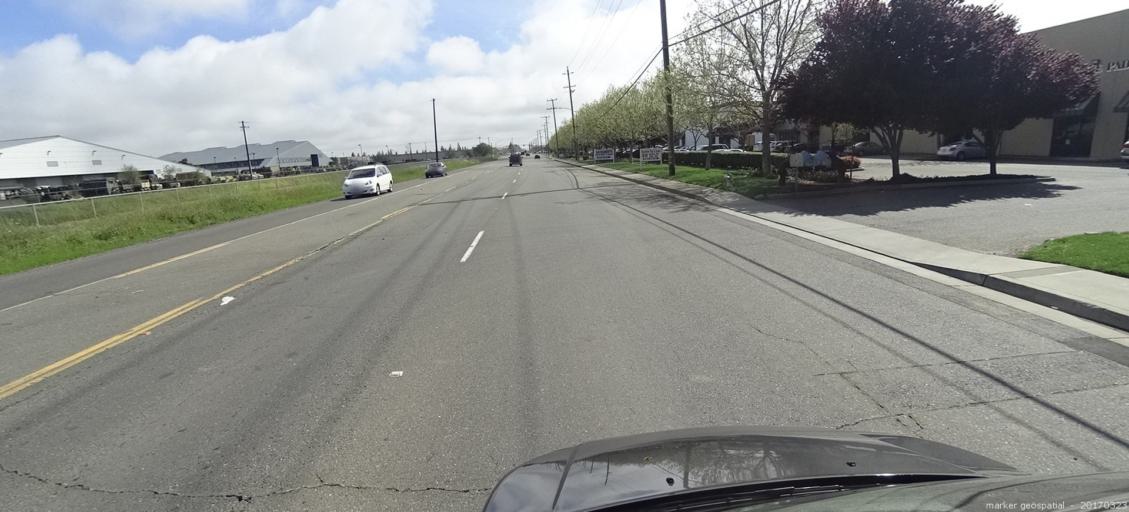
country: US
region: California
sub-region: Sacramento County
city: Florin
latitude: 38.5105
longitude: -121.3953
